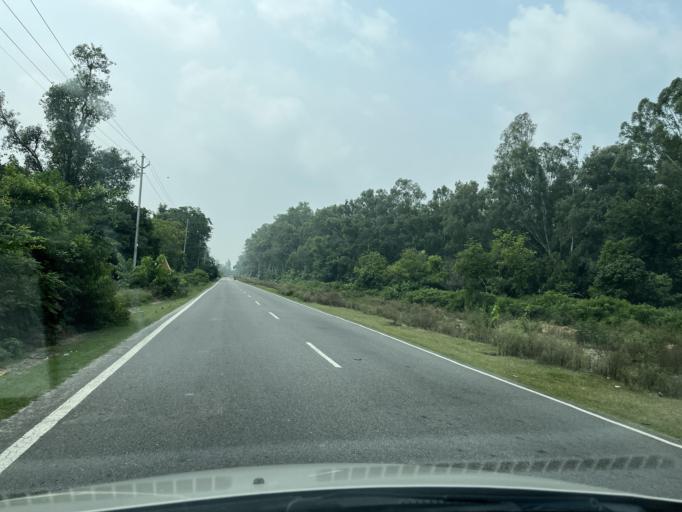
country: IN
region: Uttarakhand
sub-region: Haridwar
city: Sultanpur
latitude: 29.7565
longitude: 78.2669
